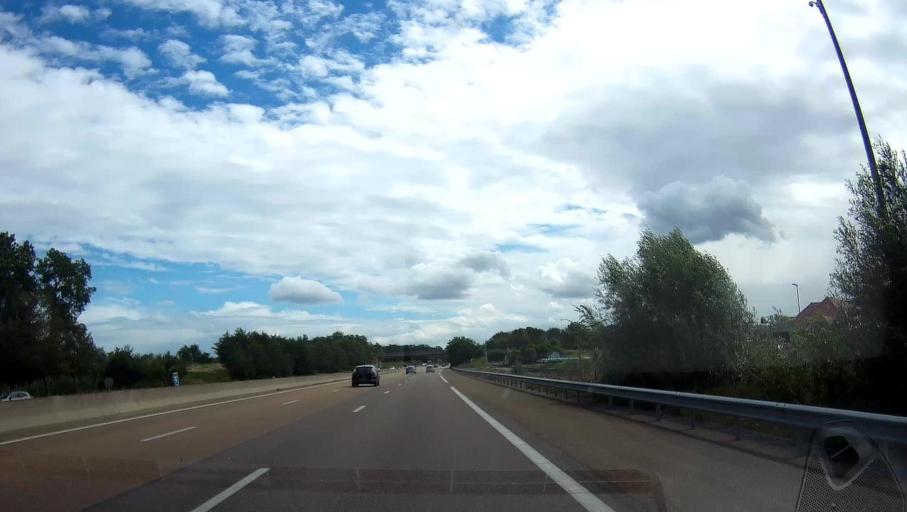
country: FR
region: Bourgogne
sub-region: Departement de la Cote-d'Or
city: Saint-Julien
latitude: 47.4228
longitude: 5.1723
